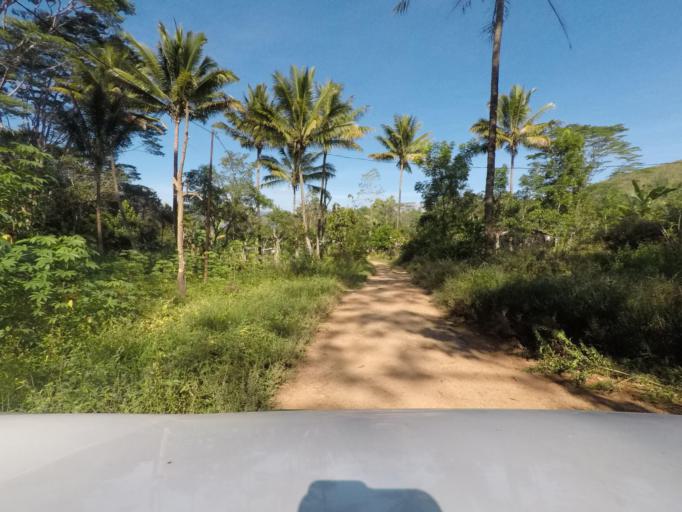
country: TL
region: Ermera
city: Gleno
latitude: -8.7097
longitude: 125.4483
